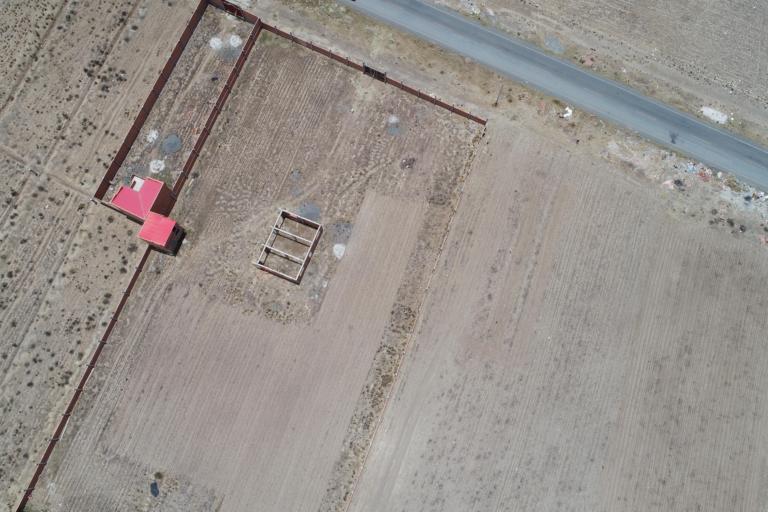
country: BO
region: La Paz
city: Achacachi
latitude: -16.0453
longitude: -68.6952
